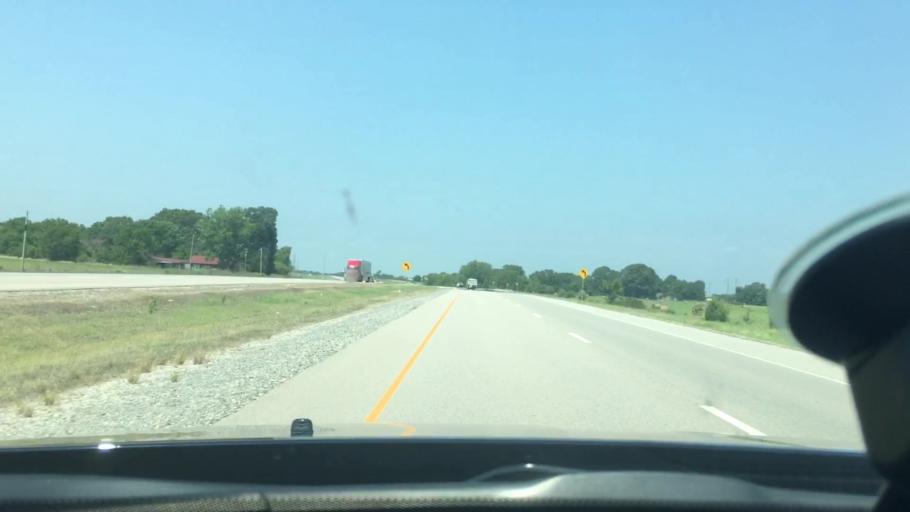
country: US
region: Oklahoma
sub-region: Atoka County
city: Atoka
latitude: 34.3333
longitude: -96.0532
